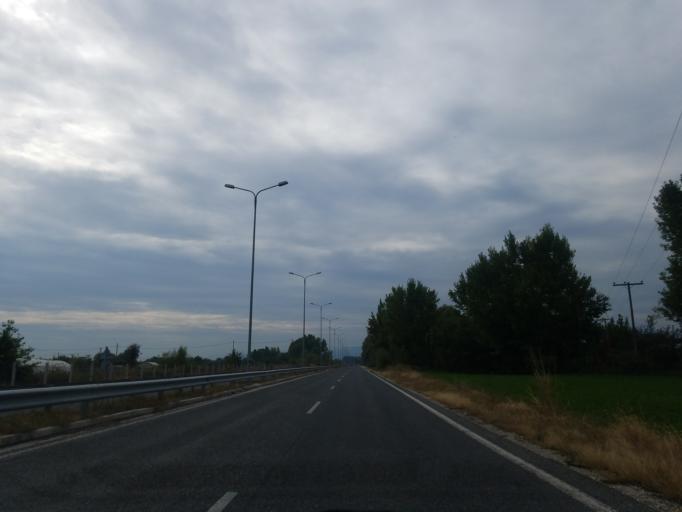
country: GR
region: Thessaly
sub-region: Trikala
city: Pyrgetos
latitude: 39.5479
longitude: 21.7348
